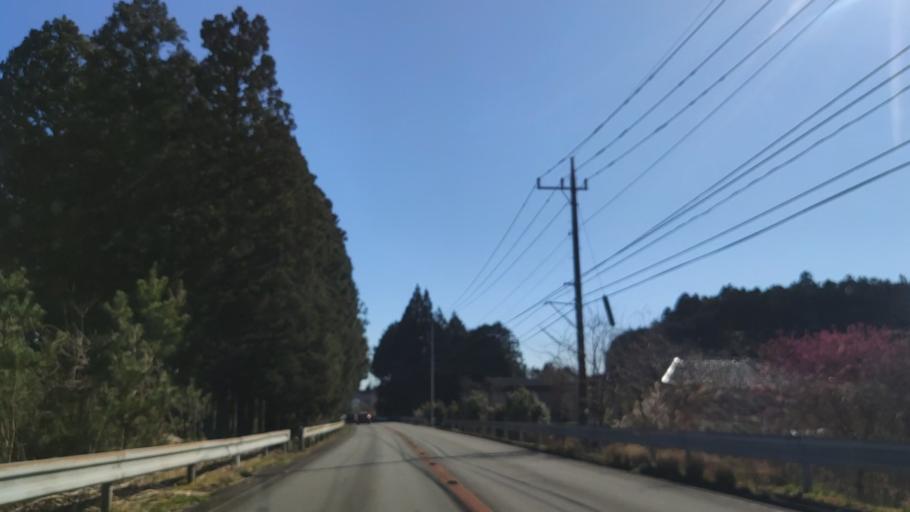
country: JP
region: Shizuoka
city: Fujinomiya
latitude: 35.3222
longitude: 138.5860
